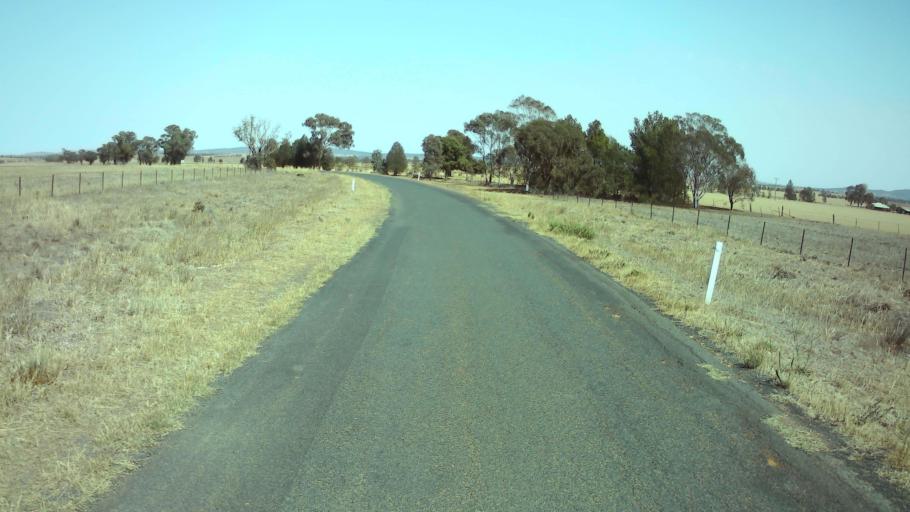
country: AU
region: New South Wales
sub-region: Weddin
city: Grenfell
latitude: -33.8612
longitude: 147.9810
